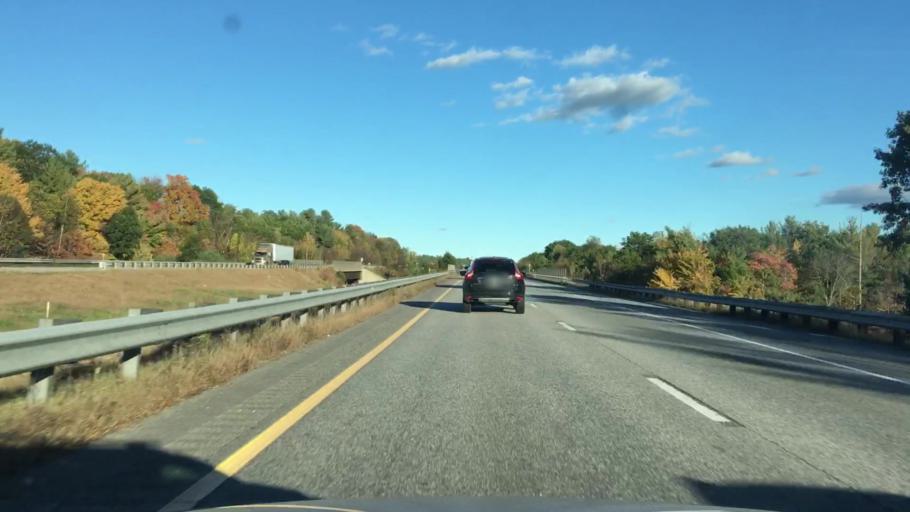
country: US
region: New Hampshire
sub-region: Rockingham County
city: Auburn
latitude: 43.0372
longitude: -71.3273
